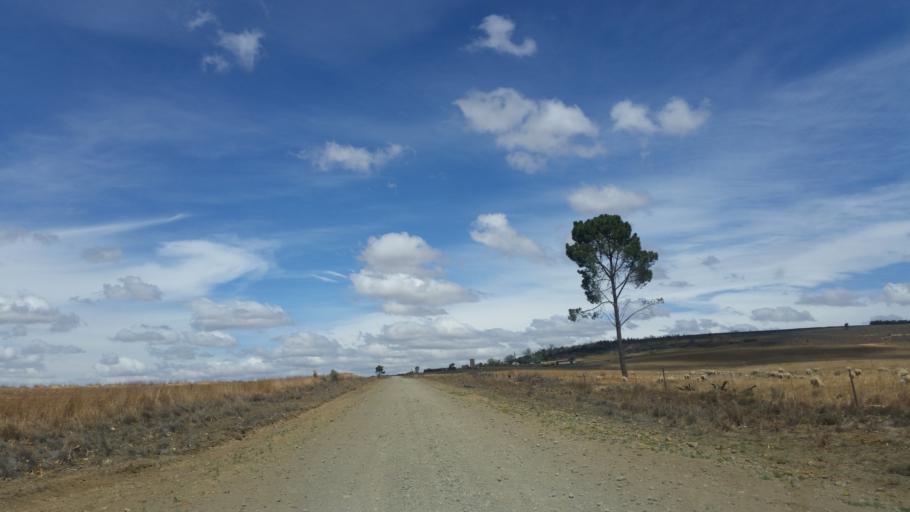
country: ZA
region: Orange Free State
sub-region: Thabo Mofutsanyana District Municipality
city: Bethlehem
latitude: -28.2439
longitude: 28.5800
